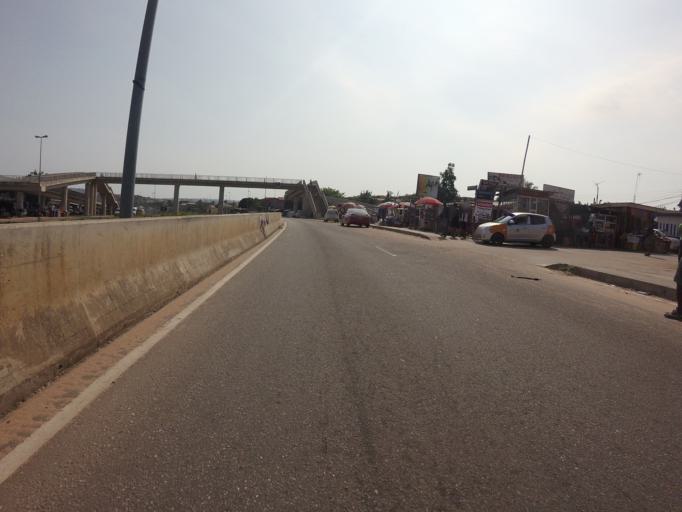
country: GH
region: Greater Accra
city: Gbawe
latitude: 5.6142
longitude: -0.2963
